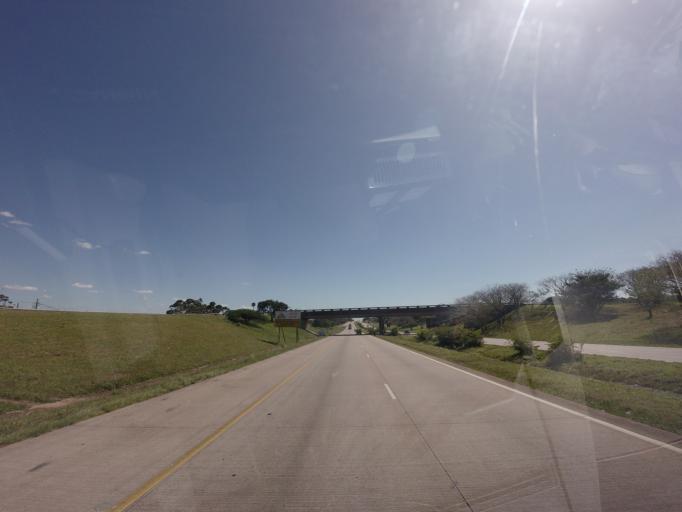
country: ZA
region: KwaZulu-Natal
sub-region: iLembe District Municipality
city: Ballitoville
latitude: -29.5036
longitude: 31.2093
